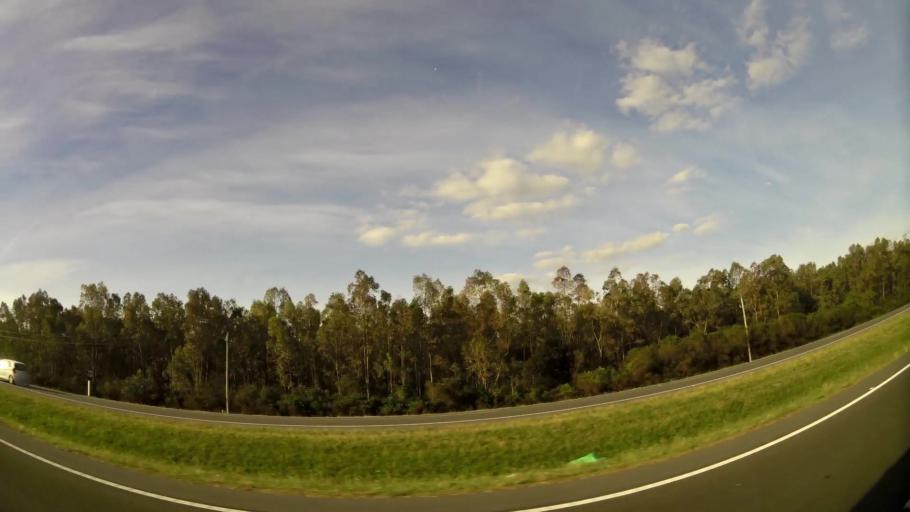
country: UY
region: Maldonado
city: Piriapolis
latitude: -34.7864
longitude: -55.3321
